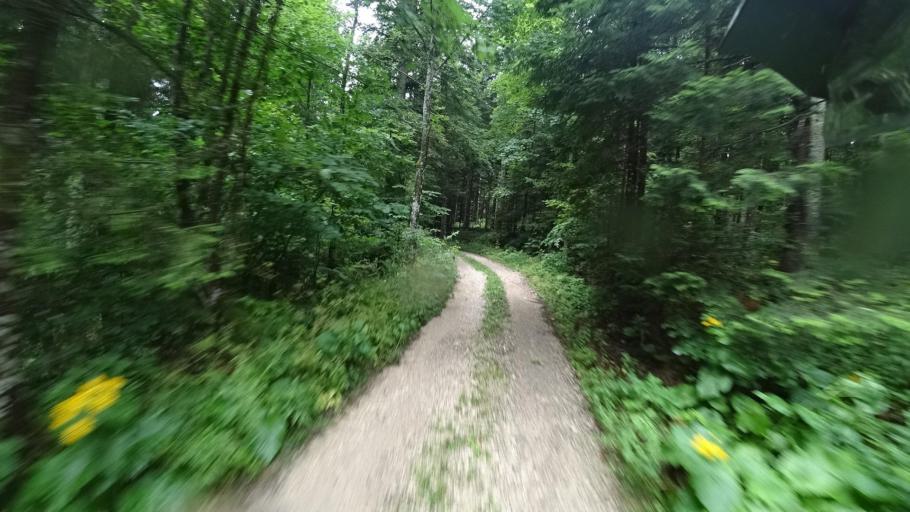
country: HR
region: Karlovacka
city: Plaski
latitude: 44.9367
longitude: 15.4105
